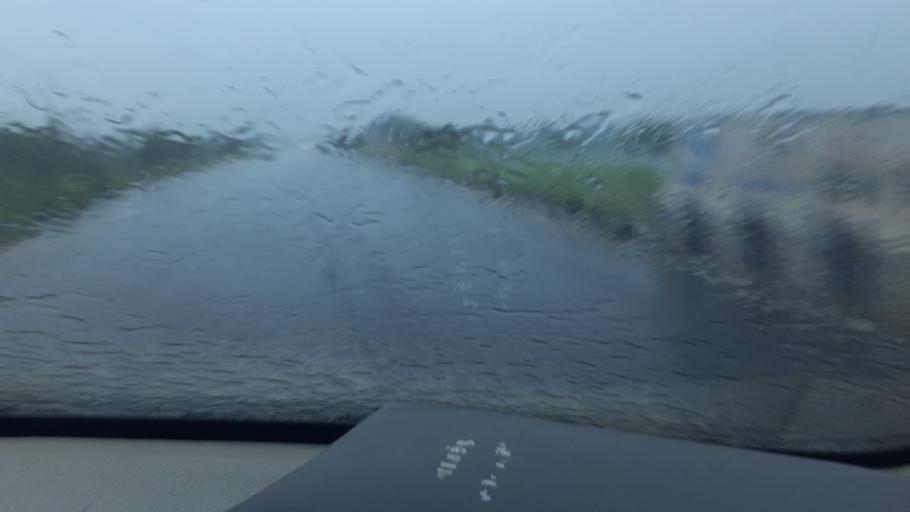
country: IN
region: Tamil Nadu
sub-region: Virudhunagar
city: Sattur
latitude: 9.4308
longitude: 77.9193
